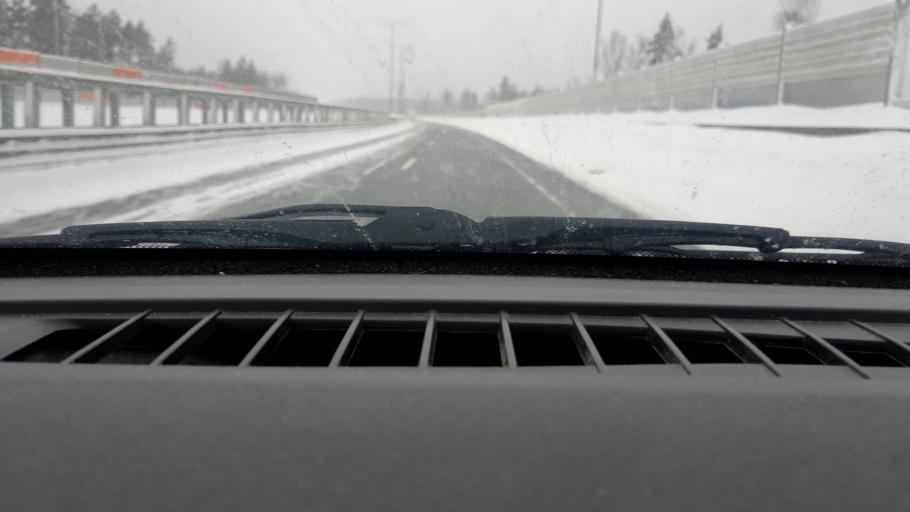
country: RU
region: Moskovskaya
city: Chernogolovka
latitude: 55.9666
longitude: 38.3548
